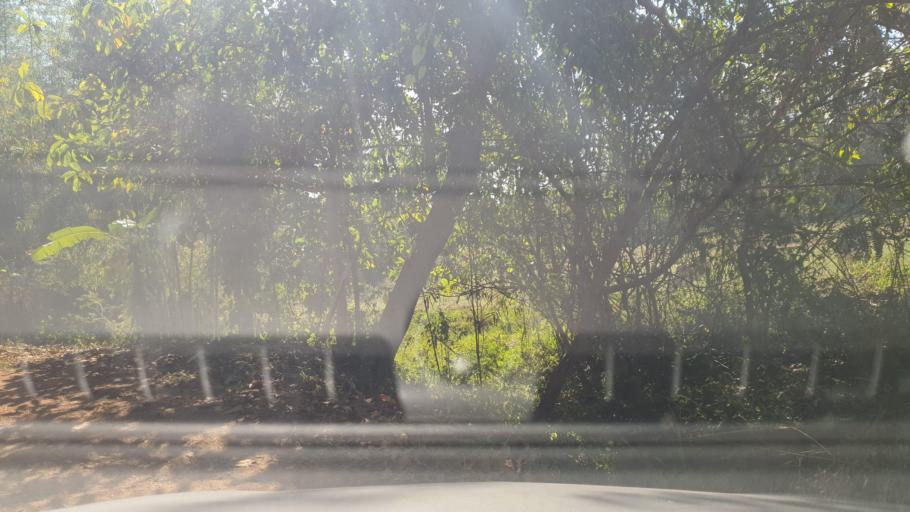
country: TH
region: Chiang Mai
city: Mae On
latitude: 18.8707
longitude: 99.2597
